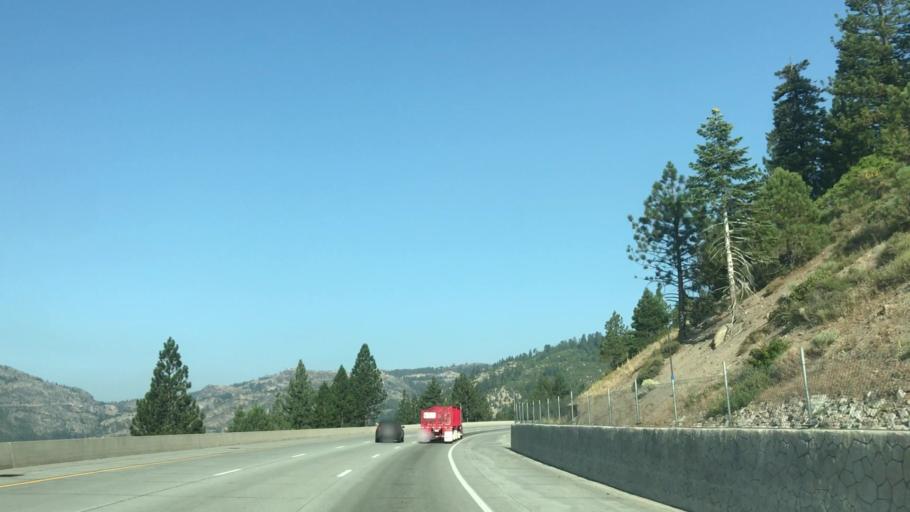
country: US
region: California
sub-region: Nevada County
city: Truckee
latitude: 39.3277
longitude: -120.2741
